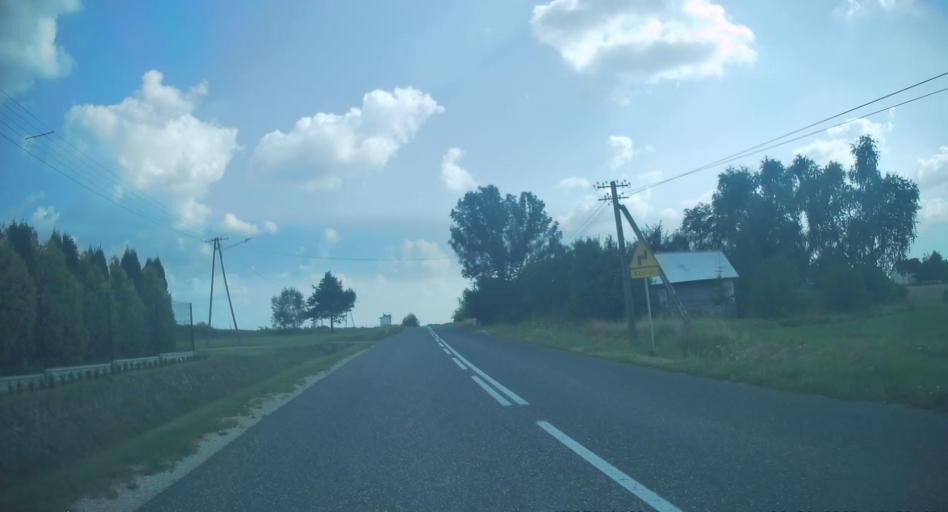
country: PL
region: Swietokrzyskie
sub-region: Powiat kielecki
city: Lopuszno
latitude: 50.9080
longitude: 20.2460
